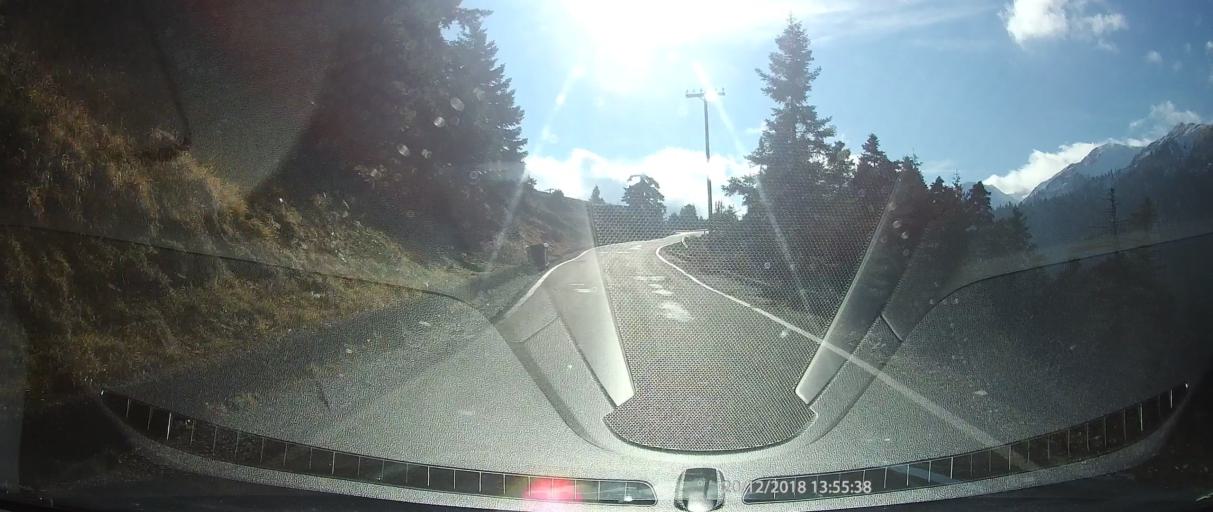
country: GR
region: West Greece
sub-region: Nomos Aitolias kai Akarnanias
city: Paravola
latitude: 38.7097
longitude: 21.6141
